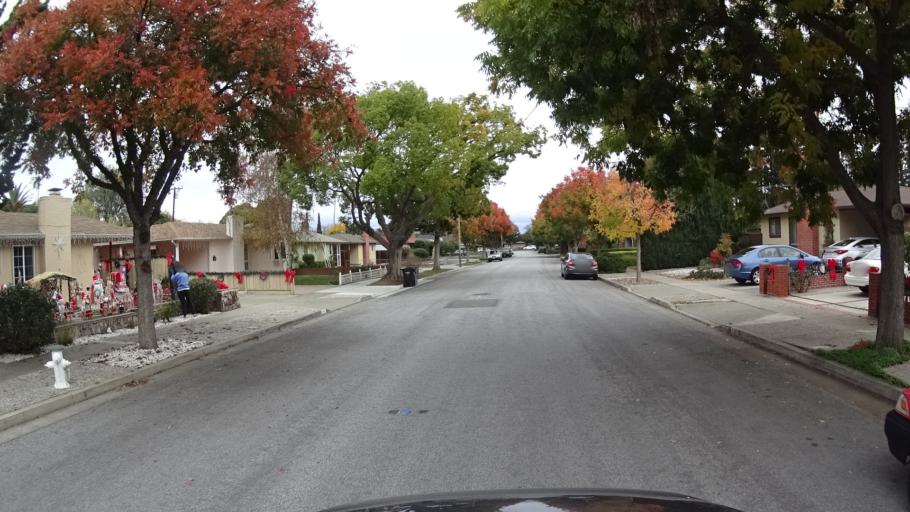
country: US
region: California
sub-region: Santa Clara County
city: Sunnyvale
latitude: 37.3610
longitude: -121.9990
